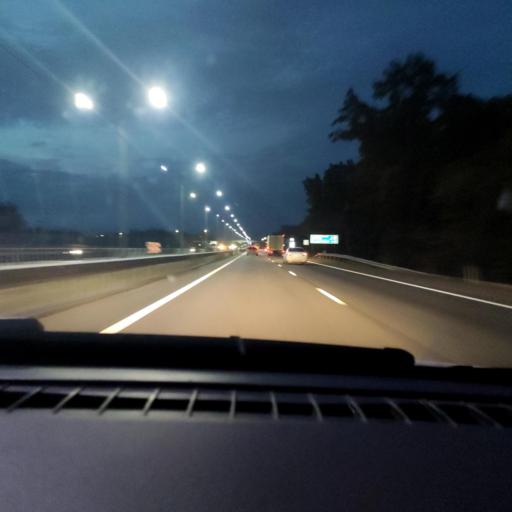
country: RU
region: Voronezj
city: Ramon'
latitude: 51.8841
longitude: 39.2175
